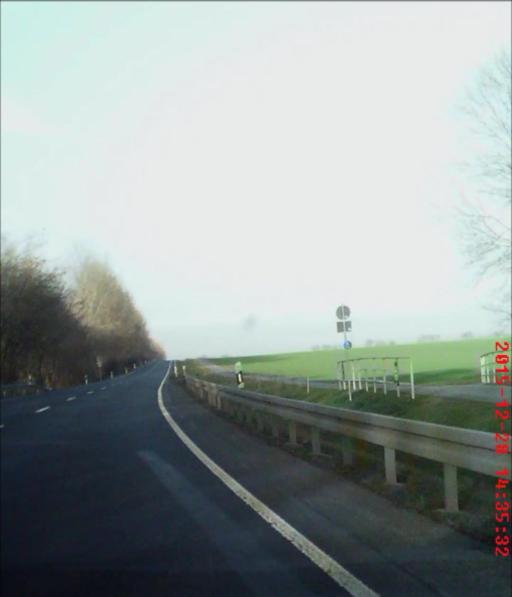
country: DE
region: Thuringia
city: Grossobringen
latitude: 51.0423
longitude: 11.3361
